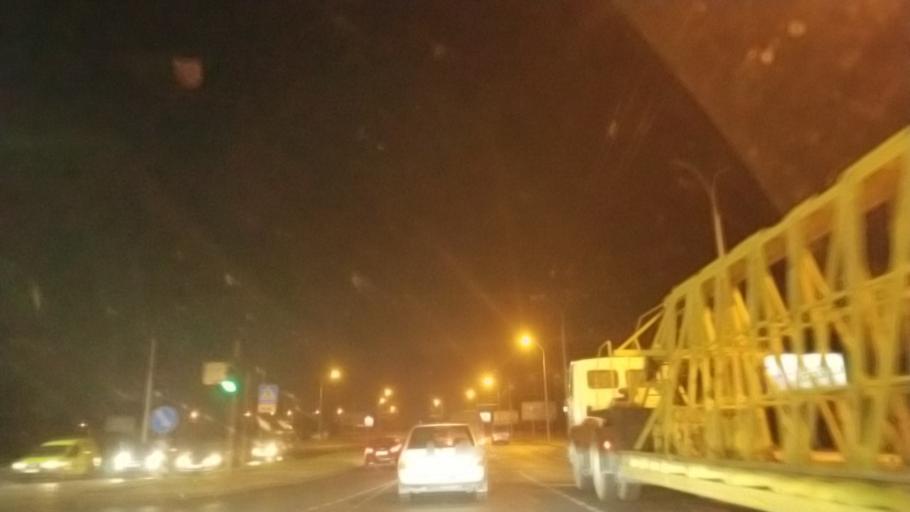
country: BY
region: Brest
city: Brest
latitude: 52.0838
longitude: 23.7719
